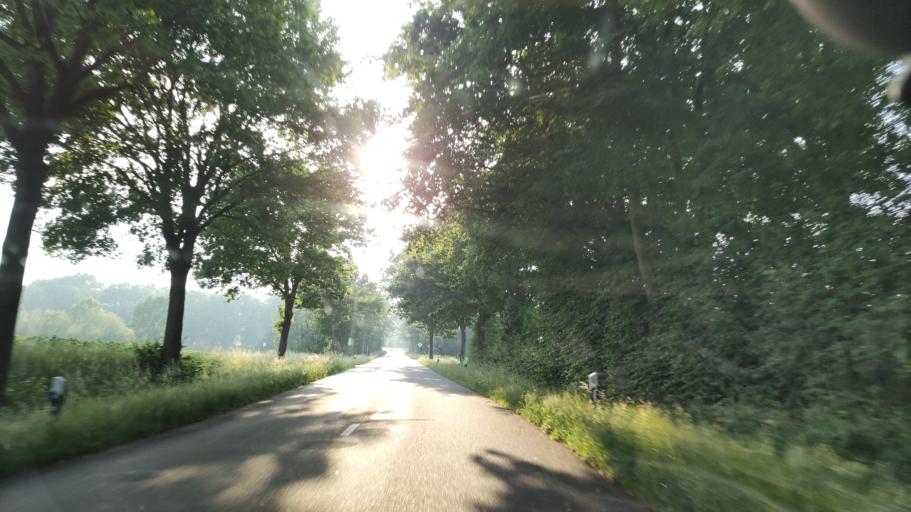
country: DE
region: Lower Saxony
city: Hanstedt Eins
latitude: 53.0317
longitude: 10.3531
